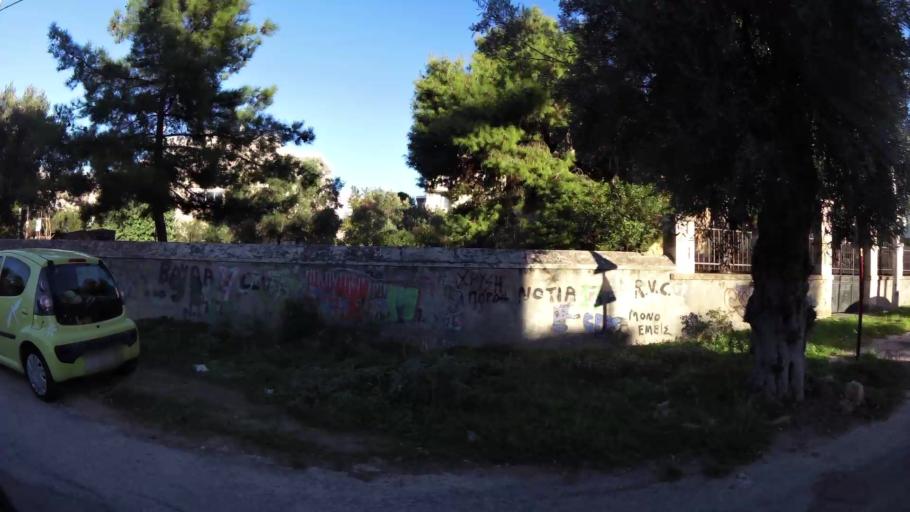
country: GR
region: Attica
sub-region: Nomarchia Athinas
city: Glyfada
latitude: 37.8568
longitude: 23.7616
